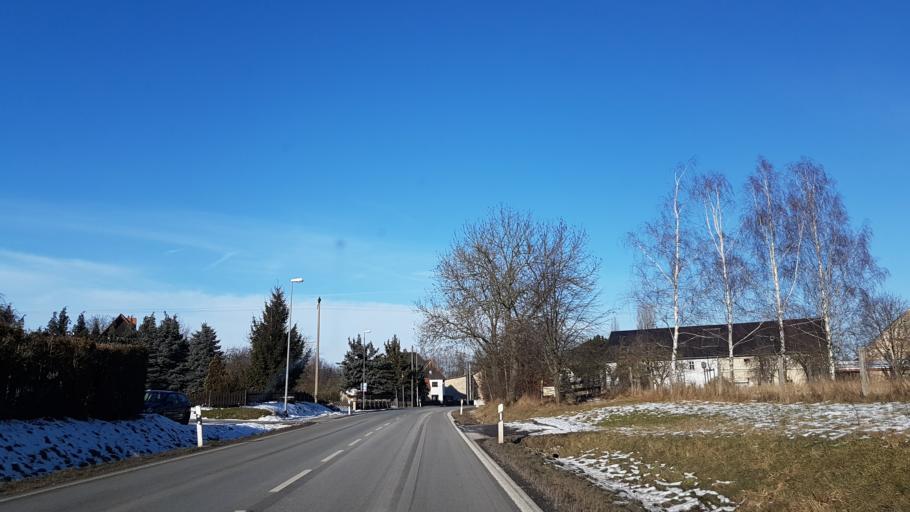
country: DE
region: Thuringia
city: Nobitz
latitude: 50.9692
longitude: 12.4979
